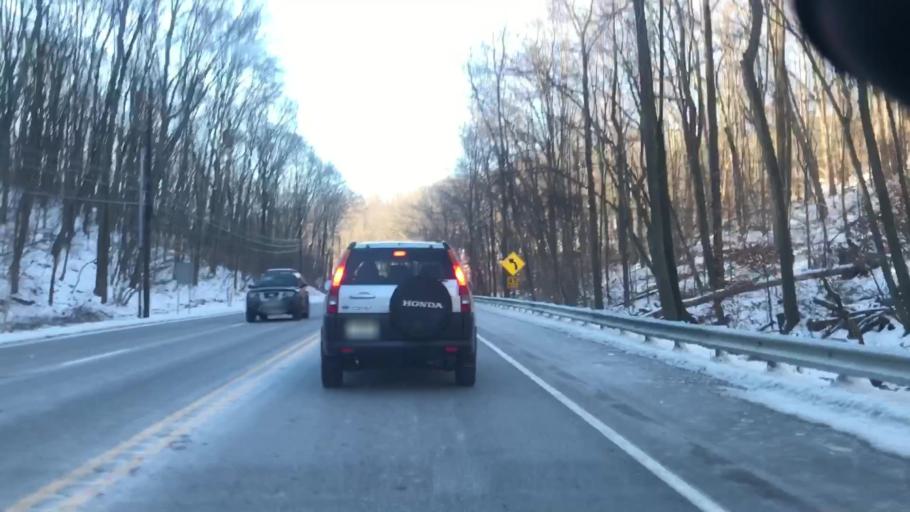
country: US
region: New Jersey
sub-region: Morris County
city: Budd Lake
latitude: 40.8574
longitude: -74.7003
